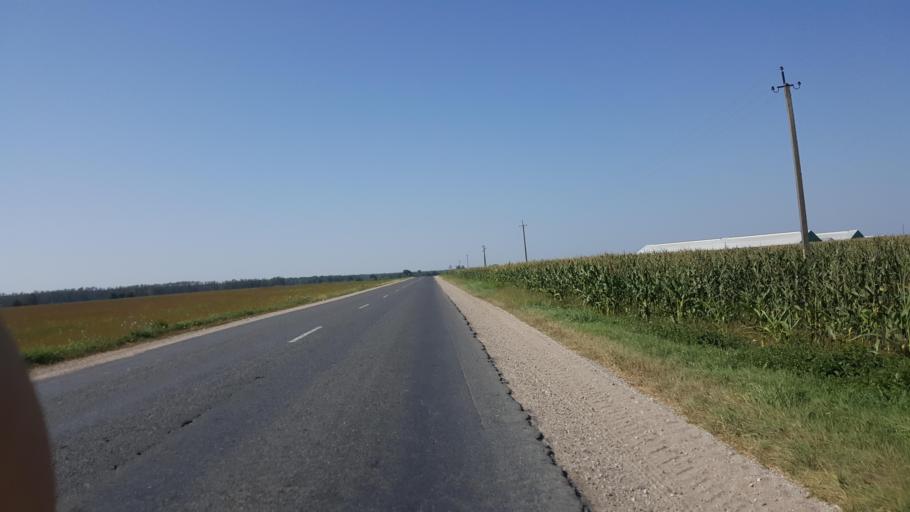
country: BY
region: Brest
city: Kamyanyets
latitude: 52.4153
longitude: 23.6110
